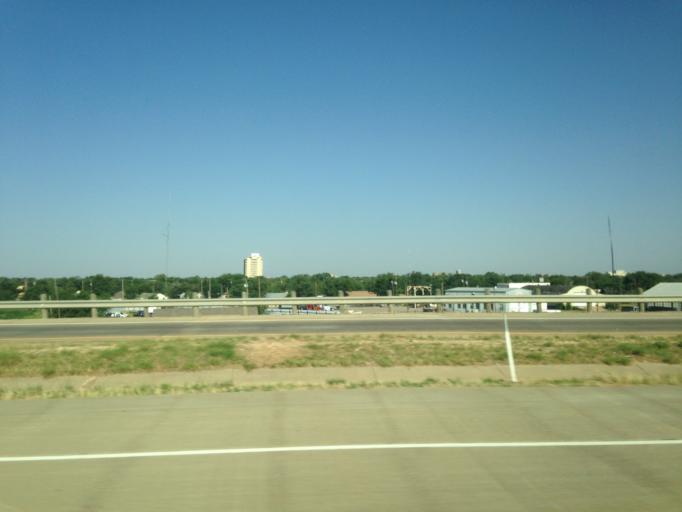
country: US
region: Texas
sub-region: Lubbock County
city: Lubbock
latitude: 33.5696
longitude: -101.8449
